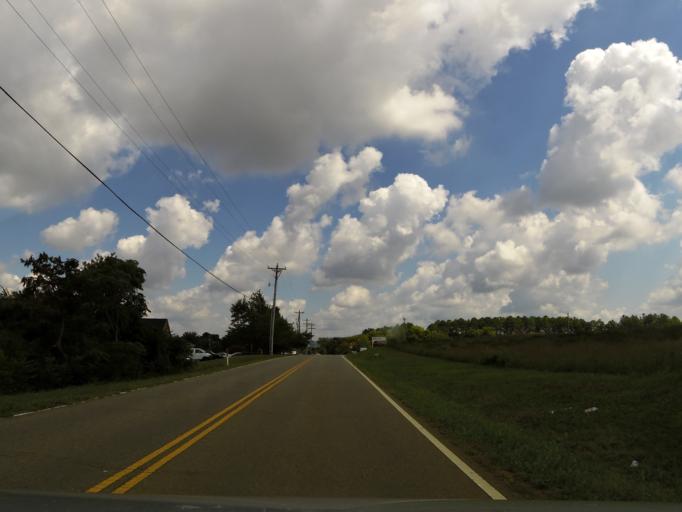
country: US
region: Tennessee
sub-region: Blount County
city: Alcoa
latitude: 35.8138
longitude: -83.9796
